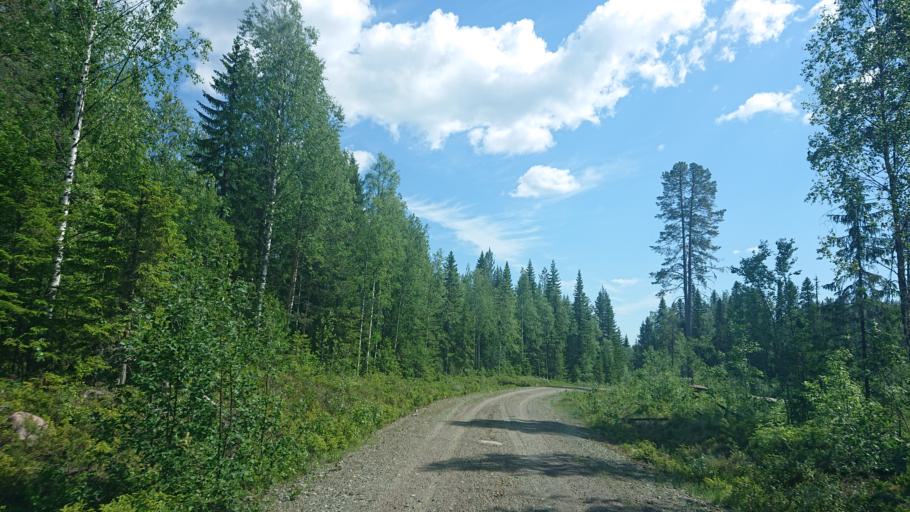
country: SE
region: Vaesternorrland
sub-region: Solleftea Kommun
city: Solleftea
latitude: 62.9321
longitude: 17.0880
